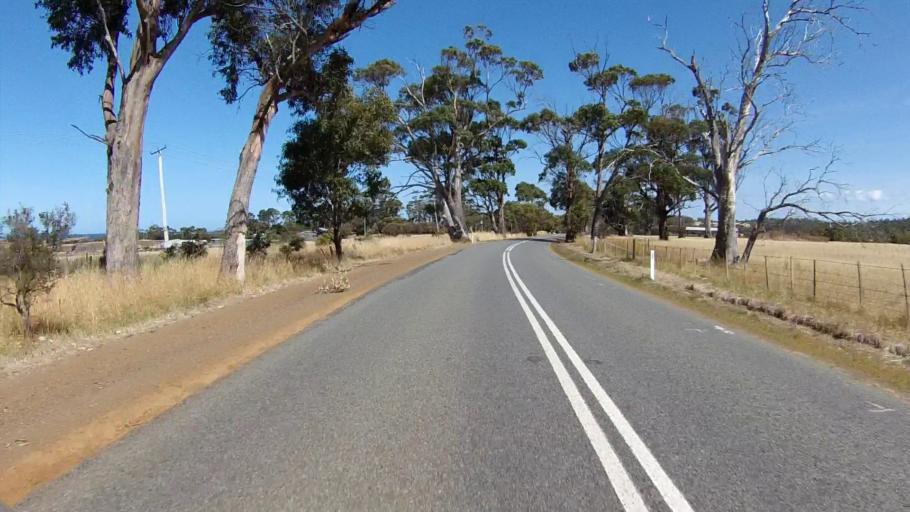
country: AU
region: Tasmania
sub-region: Sorell
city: Sorell
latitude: -42.2548
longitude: 148.0056
